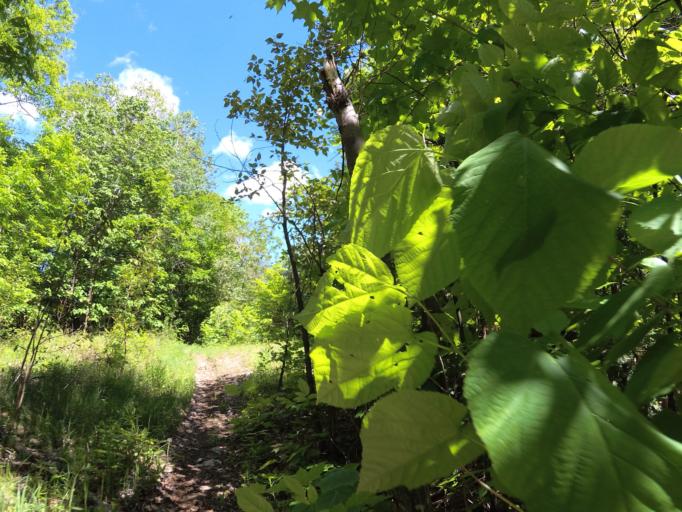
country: CA
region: Ontario
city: Renfrew
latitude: 45.0606
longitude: -76.8380
